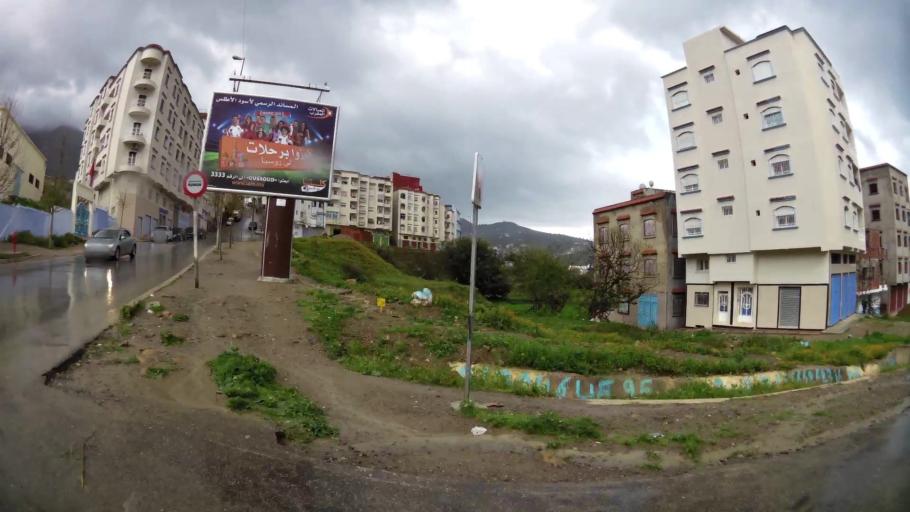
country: MA
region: Tanger-Tetouan
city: Chefchaouene
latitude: 35.1671
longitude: -5.2745
